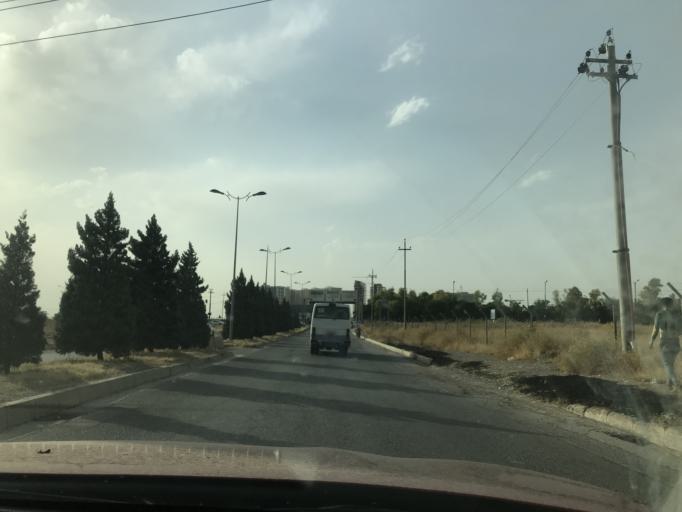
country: IQ
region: Arbil
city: Erbil
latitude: 36.1812
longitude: 43.9761
